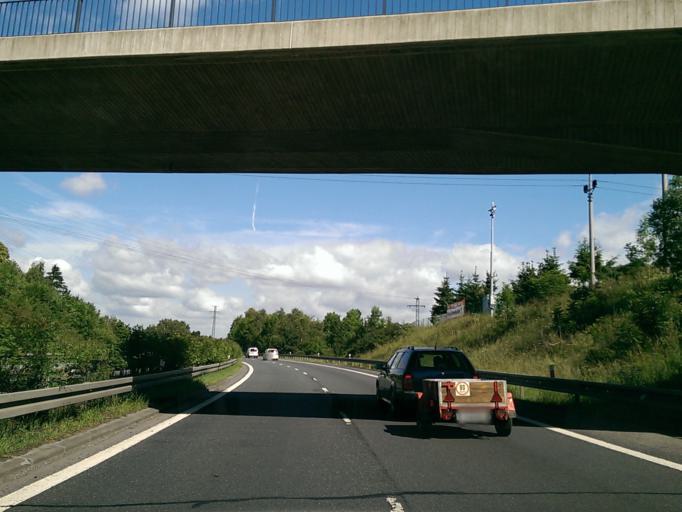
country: CZ
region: Liberecky
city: Hodkovice nad Mohelkou
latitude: 50.7074
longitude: 15.0907
